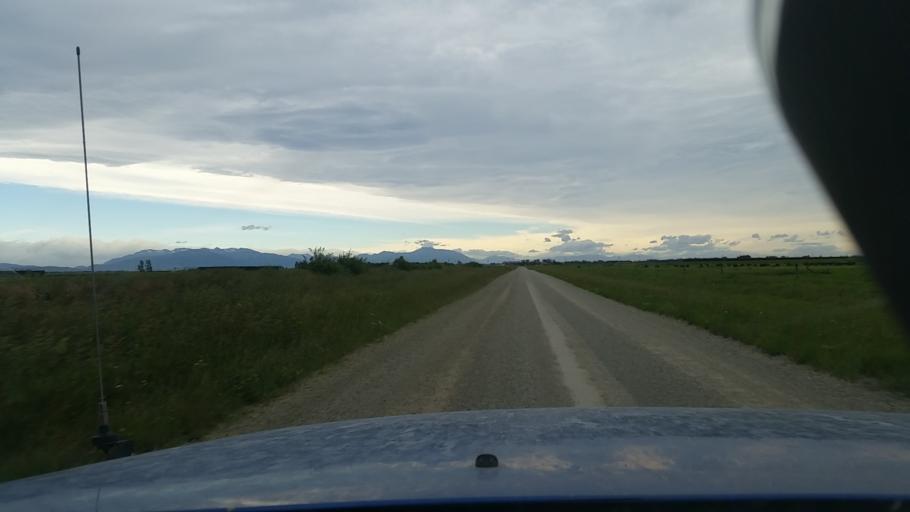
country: NZ
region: Canterbury
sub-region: Ashburton District
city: Tinwald
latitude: -43.9829
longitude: 171.5069
